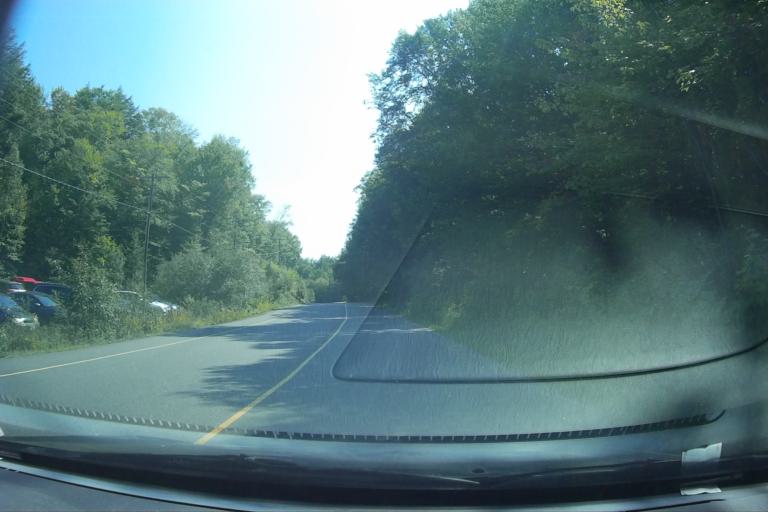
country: CA
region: Ontario
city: Huntsville
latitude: 45.5340
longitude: -78.7064
